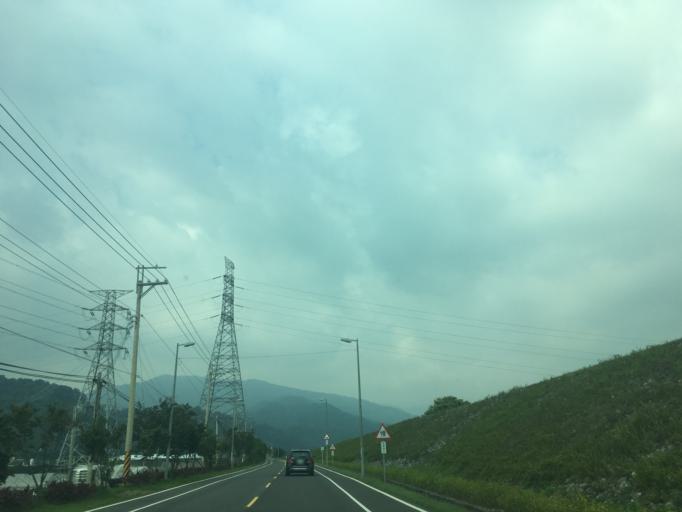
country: TW
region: Taiwan
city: Fengyuan
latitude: 24.2918
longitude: 120.8632
